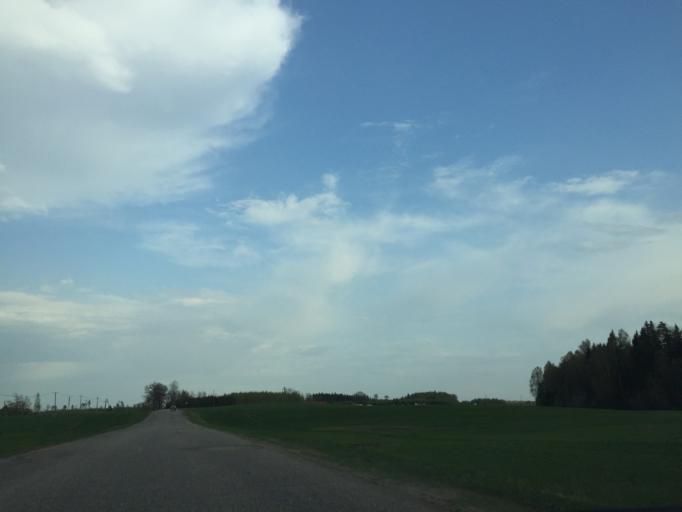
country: LV
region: Malpils
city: Malpils
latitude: 57.0088
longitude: 24.9026
